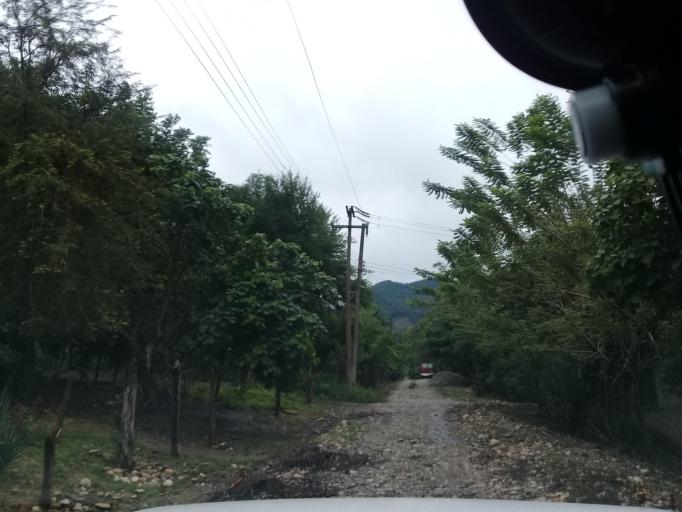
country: MX
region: Veracruz
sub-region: Chalma
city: San Pedro Coyutla
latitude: 21.2213
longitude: -98.4275
